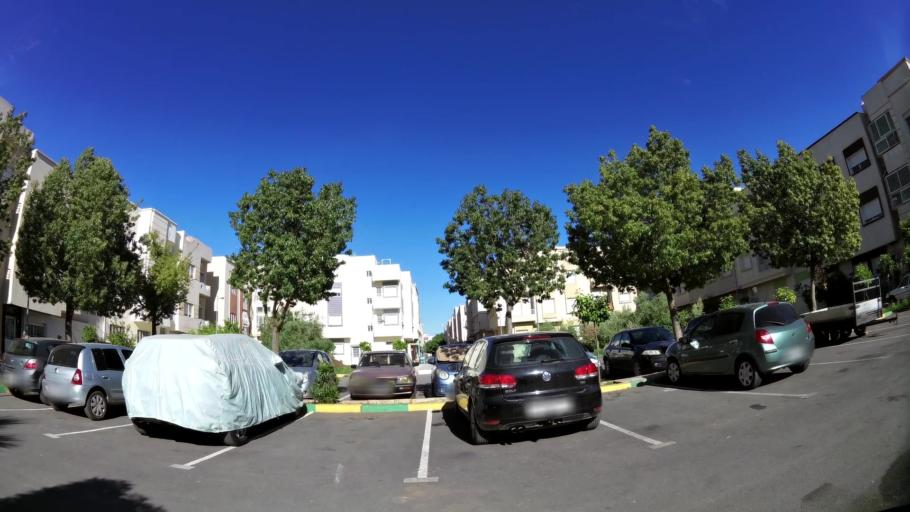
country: MA
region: Fes-Boulemane
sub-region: Fes
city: Fes
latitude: 34.0058
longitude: -5.0157
